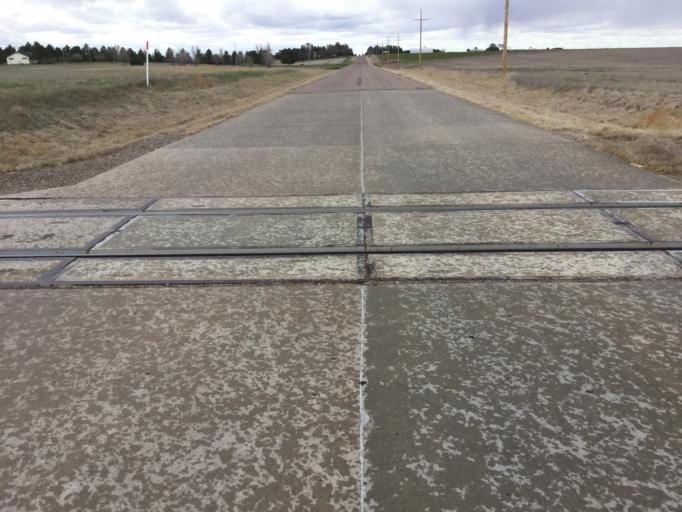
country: US
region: Kansas
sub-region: Sherman County
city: Goodland
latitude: 39.3405
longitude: -101.7823
